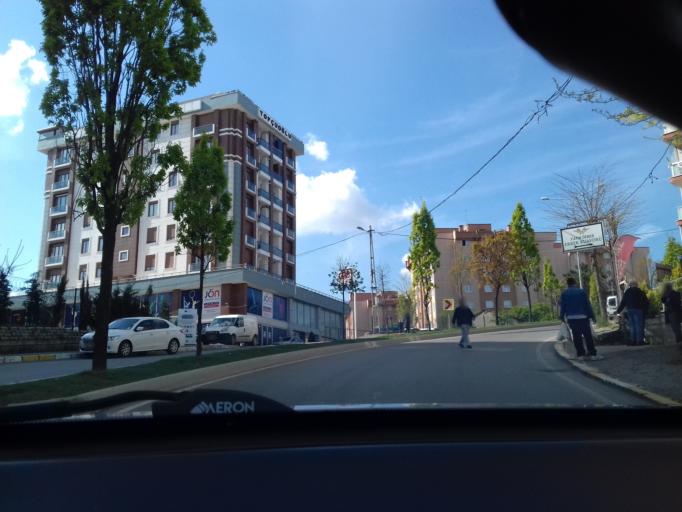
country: TR
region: Istanbul
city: Pendik
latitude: 40.9064
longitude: 29.2787
